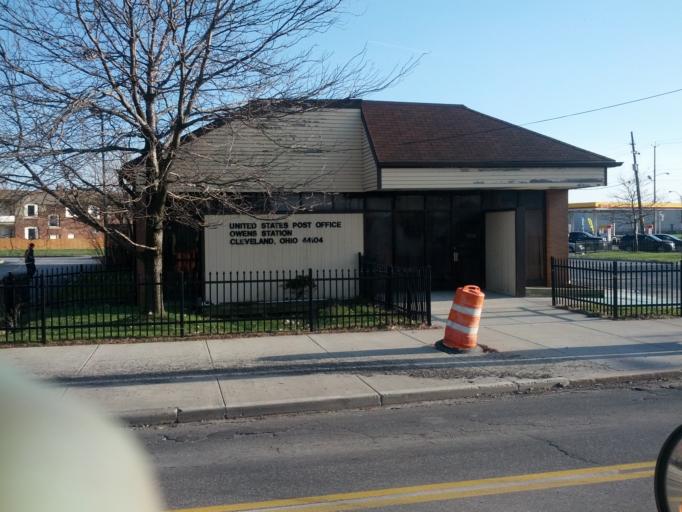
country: US
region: Ohio
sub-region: Cuyahoga County
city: Newburgh Heights
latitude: 41.4881
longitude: -81.6506
